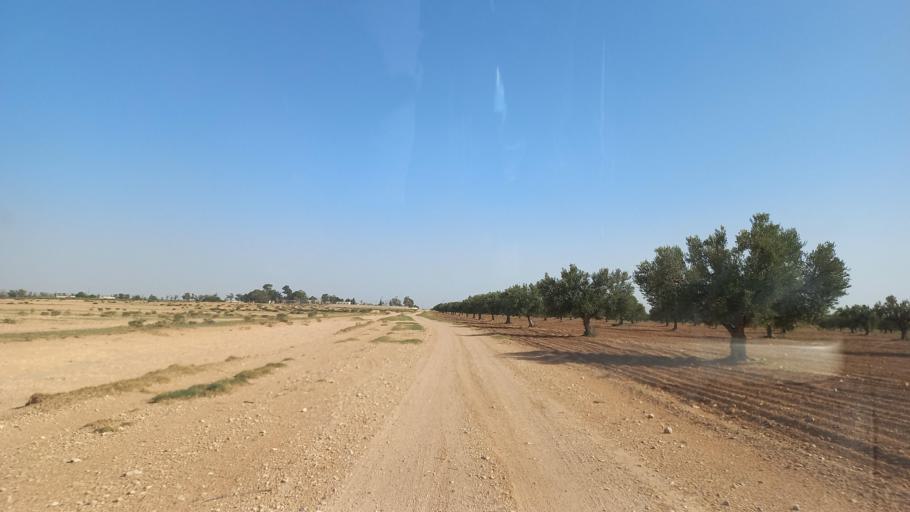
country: TN
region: Al Qasrayn
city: Kasserine
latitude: 35.3010
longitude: 9.0270
